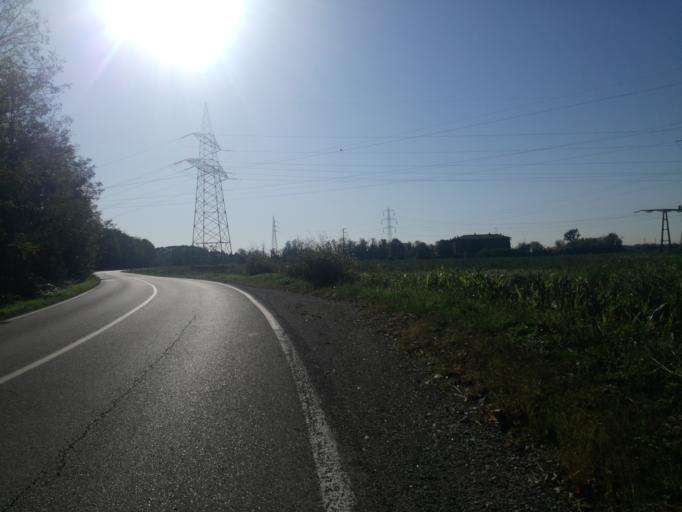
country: IT
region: Lombardy
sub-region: Provincia di Monza e Brianza
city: Cornate d'Adda
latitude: 45.6380
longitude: 9.4870
